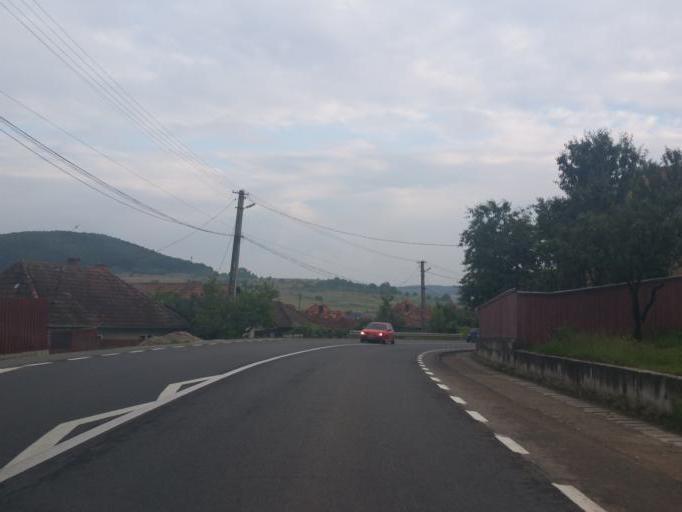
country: RO
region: Cluj
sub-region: Comuna Sanpaul
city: Sanpaul
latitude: 46.9032
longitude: 23.4174
